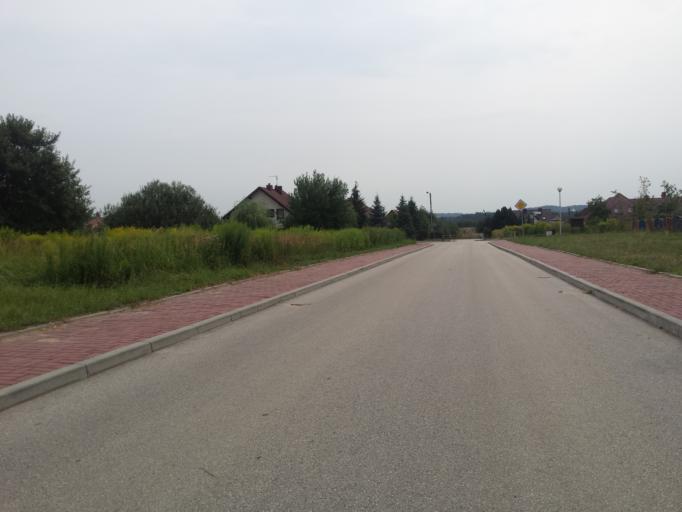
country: PL
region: Swietokrzyskie
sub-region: Powiat kielecki
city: Morawica
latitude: 50.7693
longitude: 20.6311
